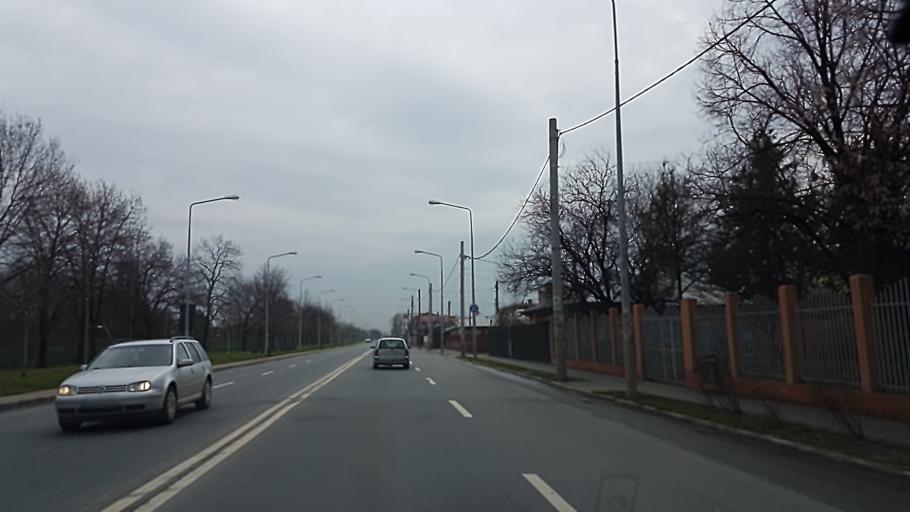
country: RO
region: Ilfov
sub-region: Comuna Pantelimon
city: Pantelimon
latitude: 44.4359
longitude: 26.2016
